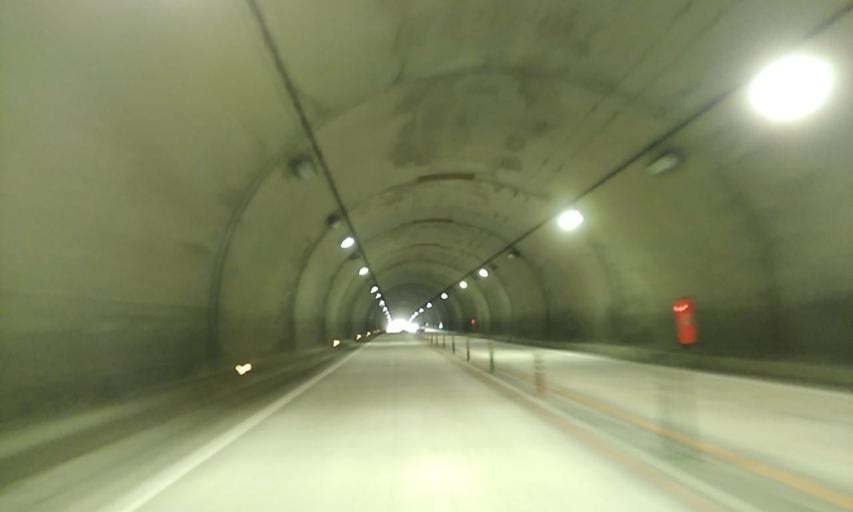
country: JP
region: Wakayama
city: Shingu
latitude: 33.5964
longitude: 135.9157
